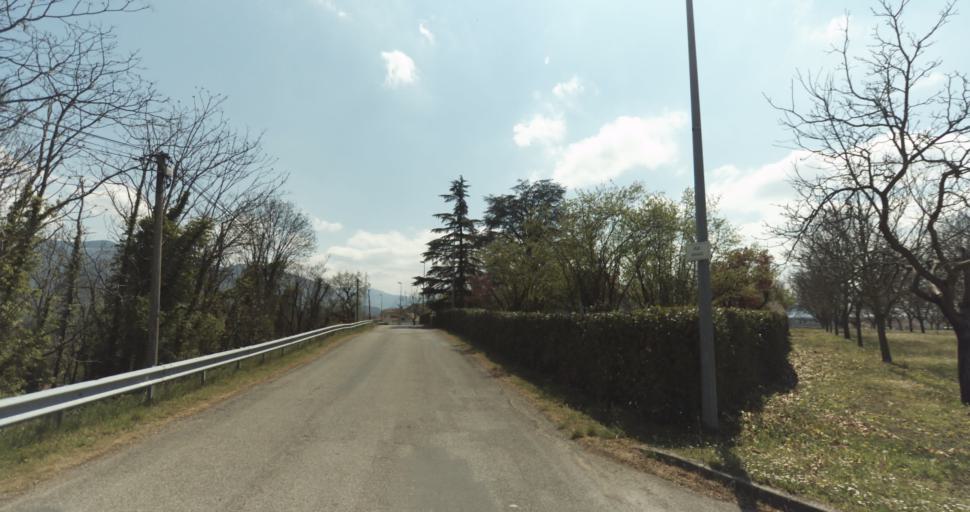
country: FR
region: Rhone-Alpes
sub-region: Departement de l'Isere
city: Saint-Marcellin
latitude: 45.1342
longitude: 5.3228
